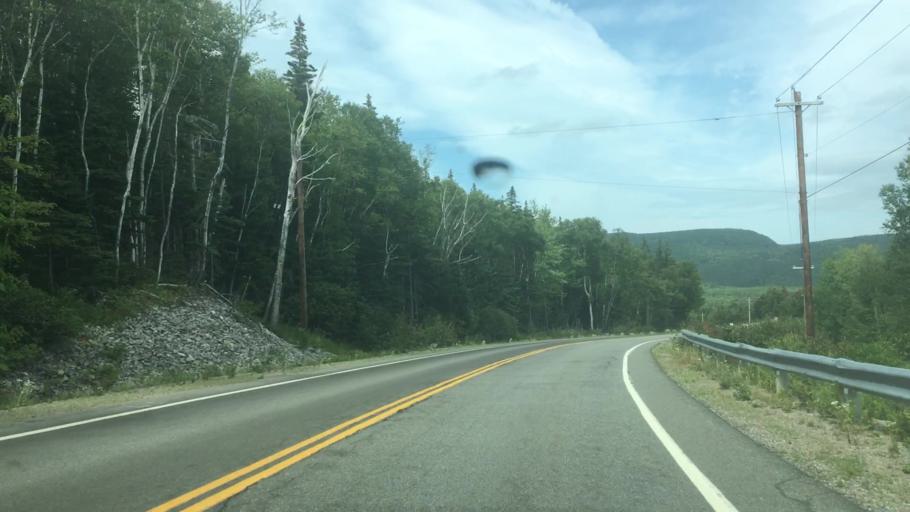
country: CA
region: Nova Scotia
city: Sydney Mines
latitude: 46.5391
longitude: -60.4141
